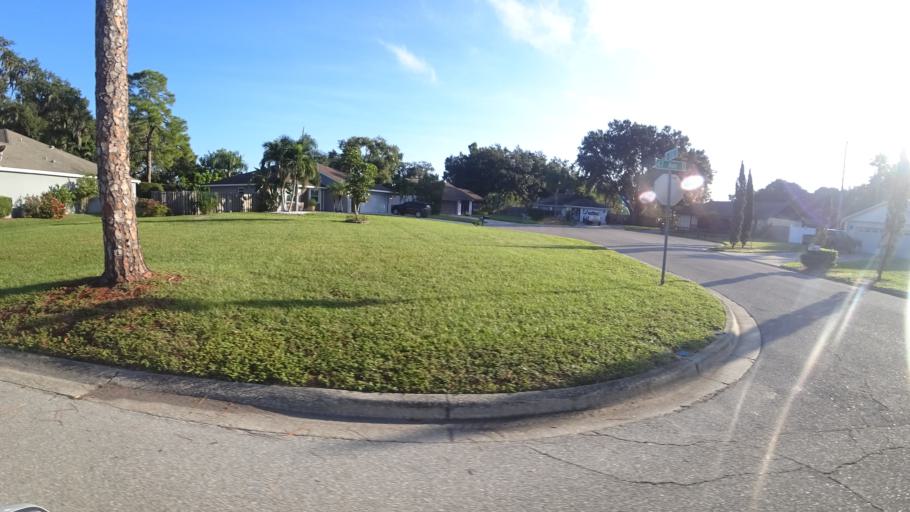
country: US
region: Florida
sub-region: Manatee County
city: Samoset
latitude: 27.4560
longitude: -82.5247
